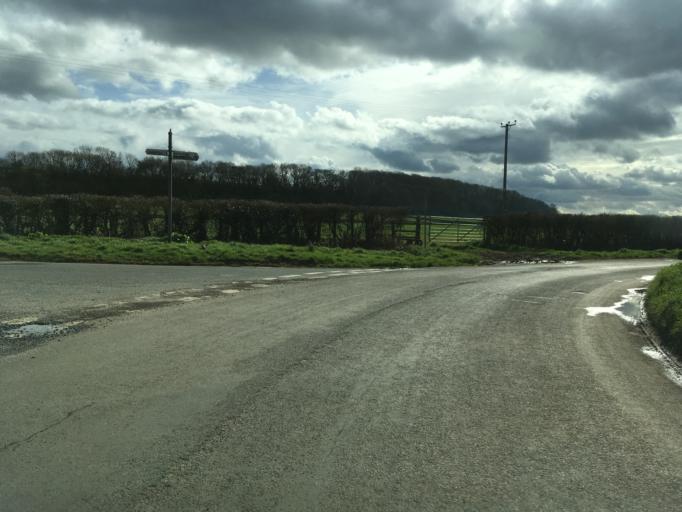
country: GB
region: England
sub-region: Gloucestershire
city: Mitcheldean
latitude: 51.8328
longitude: -2.3948
